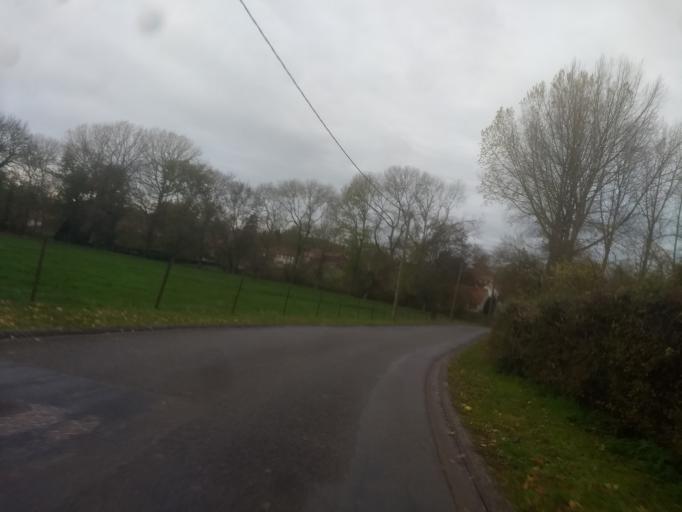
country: FR
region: Nord-Pas-de-Calais
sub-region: Departement du Pas-de-Calais
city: Riviere
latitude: 50.2352
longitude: 2.6953
